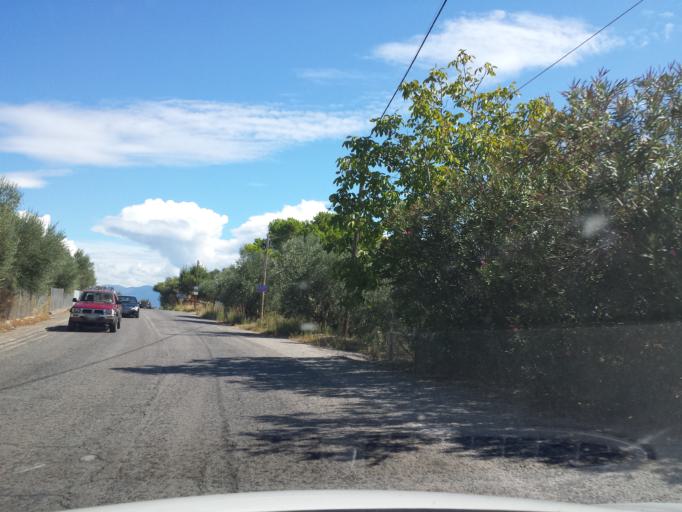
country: GR
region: Peloponnese
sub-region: Nomos Messinias
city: Vlakhopoulon
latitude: 37.0049
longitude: 21.8847
